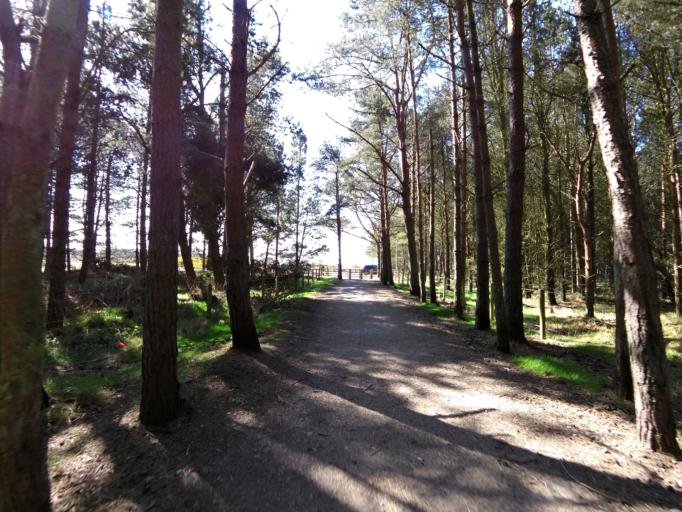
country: GB
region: Scotland
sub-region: Angus
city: Montrose
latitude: 56.7399
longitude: -2.4520
